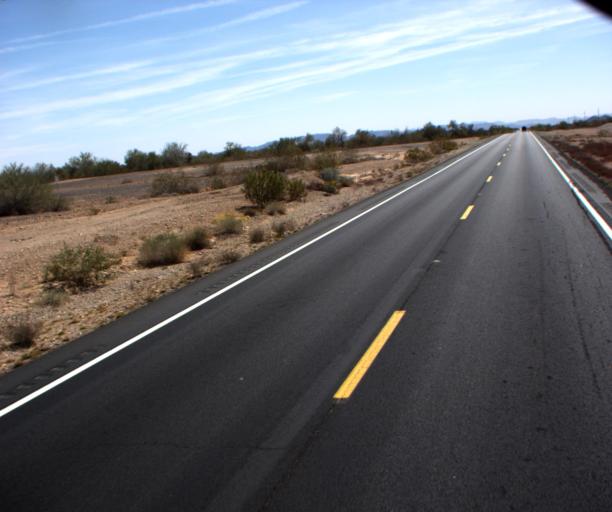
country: US
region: Arizona
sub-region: Yuma County
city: Wellton
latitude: 32.9928
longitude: -114.2872
